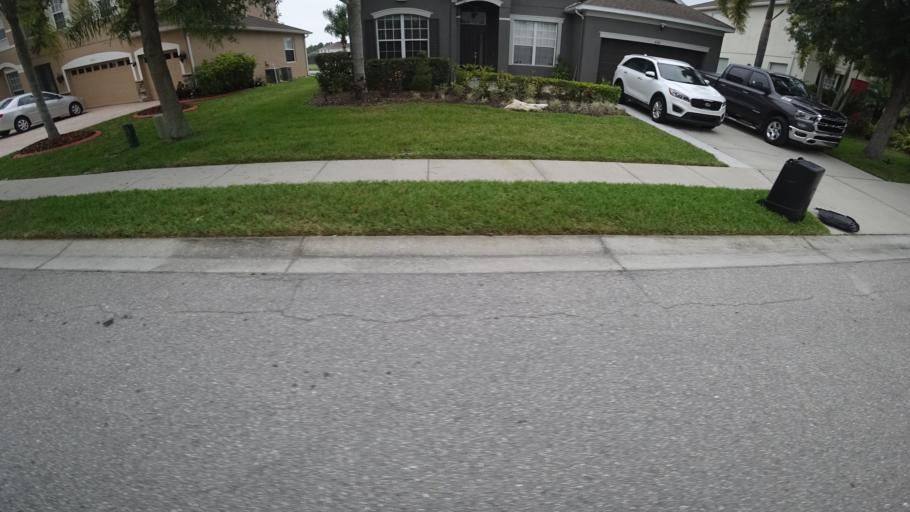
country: US
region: Florida
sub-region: Manatee County
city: Samoset
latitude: 27.4342
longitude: -82.5095
